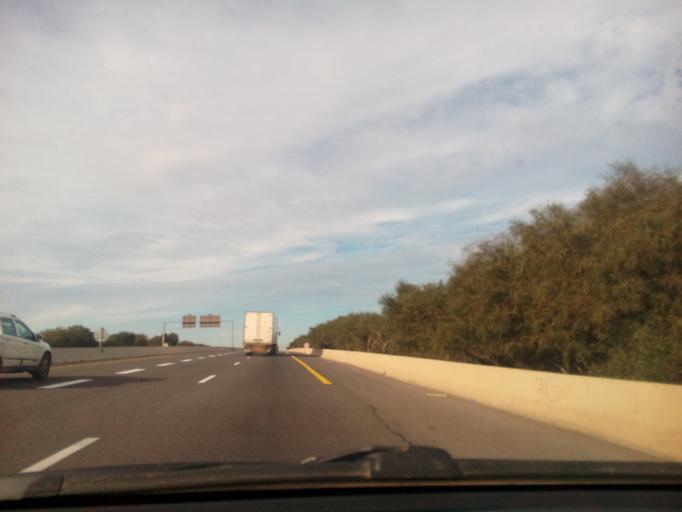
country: DZ
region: Mascara
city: Sig
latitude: 35.5420
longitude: -0.3475
